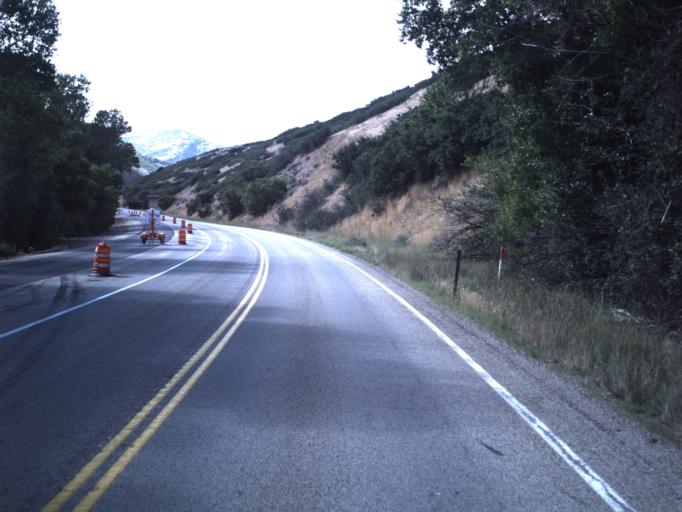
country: US
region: Utah
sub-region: Wasatch County
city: Heber
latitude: 40.4193
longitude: -111.3356
